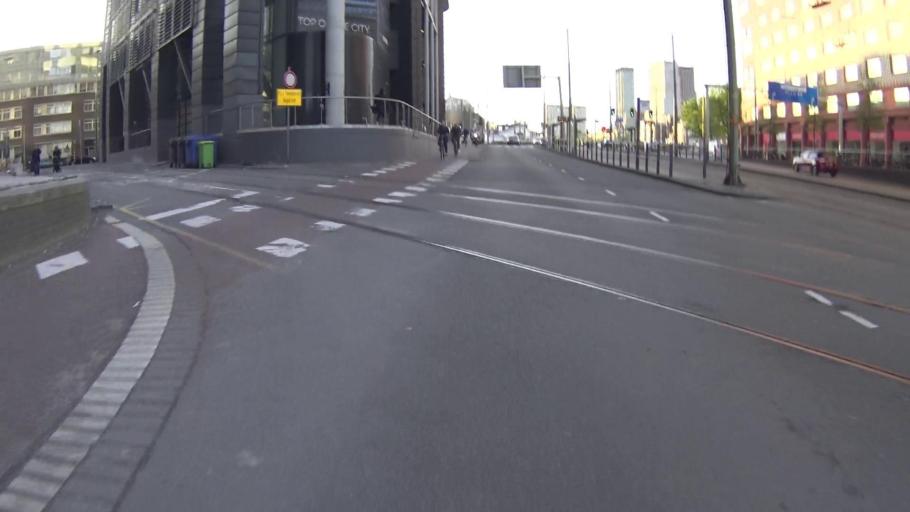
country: NL
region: South Holland
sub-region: Gemeente Den Haag
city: The Hague
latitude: 52.0712
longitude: 4.3247
